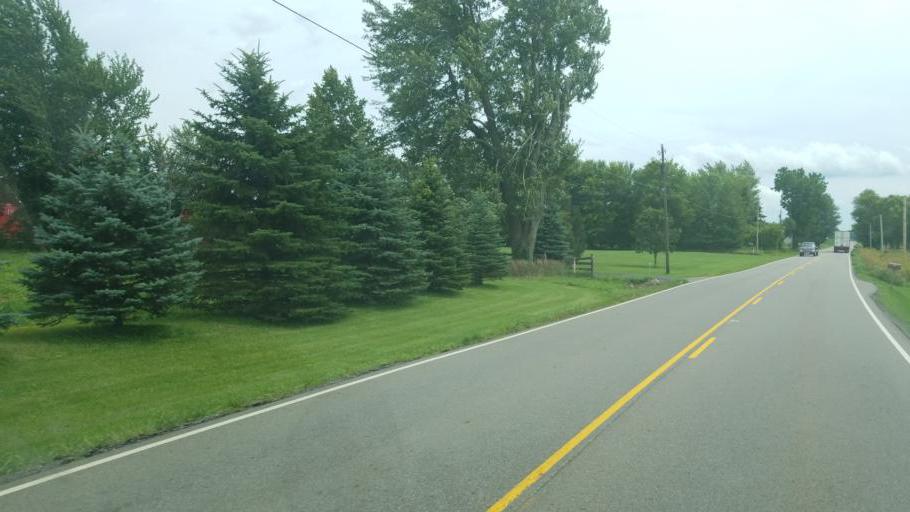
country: US
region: Ohio
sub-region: Licking County
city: Utica
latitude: 40.2469
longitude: -82.5185
